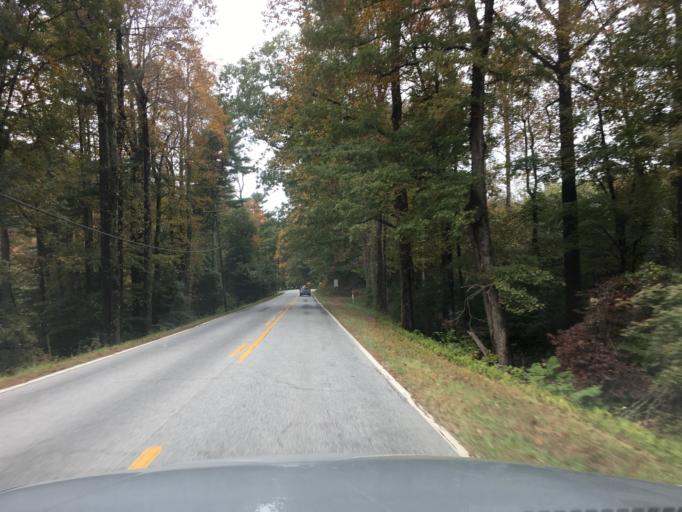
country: US
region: North Carolina
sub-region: Henderson County
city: Flat Rock
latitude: 35.2514
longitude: -82.4320
